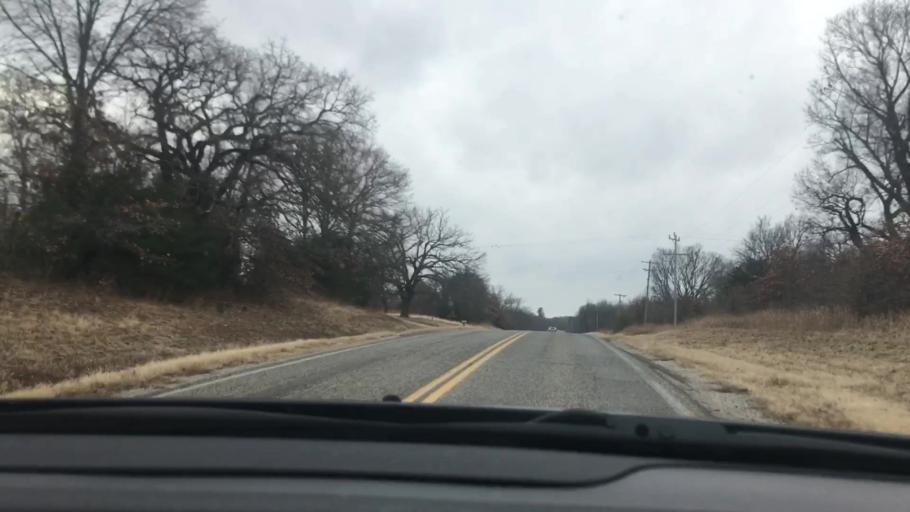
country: US
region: Oklahoma
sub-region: Johnston County
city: Tishomingo
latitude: 34.2204
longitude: -96.6362
